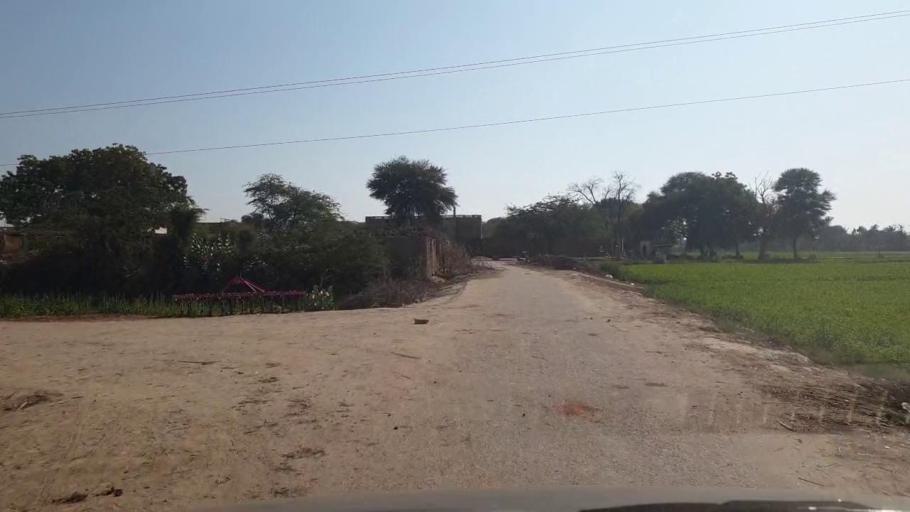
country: PK
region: Sindh
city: Shahpur Chakar
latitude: 26.1475
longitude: 68.6501
